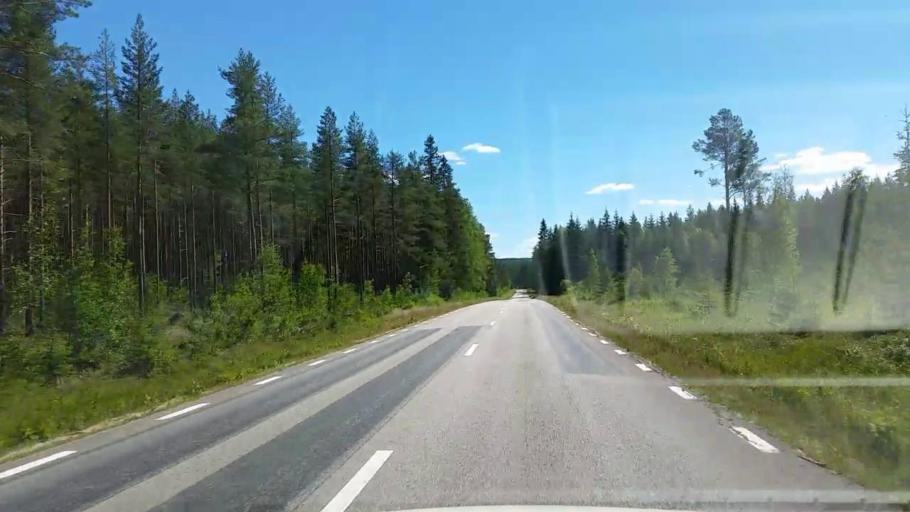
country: SE
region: Gaevleborg
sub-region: Ovanakers Kommun
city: Edsbyn
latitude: 61.3459
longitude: 15.8184
